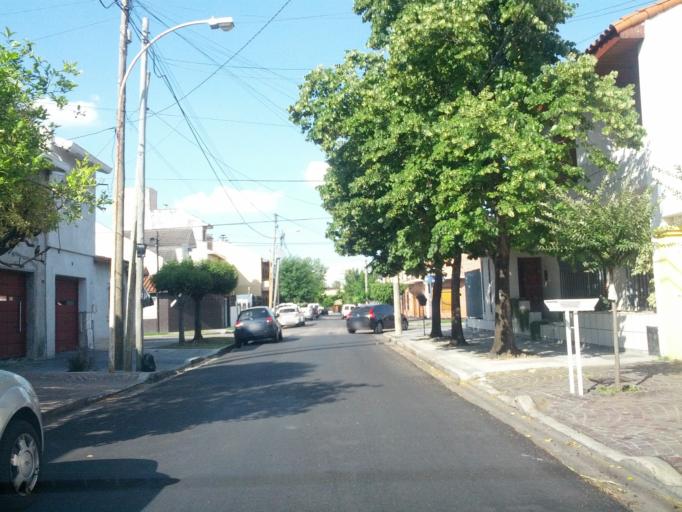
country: AR
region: Buenos Aires
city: San Justo
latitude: -34.6530
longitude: -58.5622
